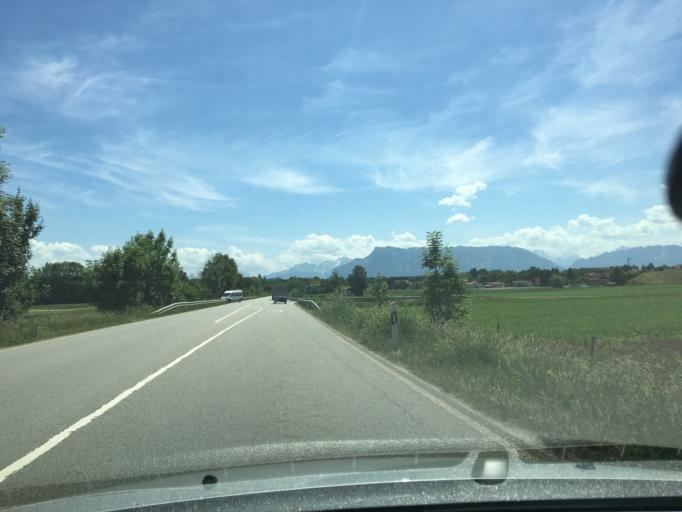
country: DE
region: Bavaria
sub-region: Upper Bavaria
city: Freilassing
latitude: 47.8829
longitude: 12.9681
